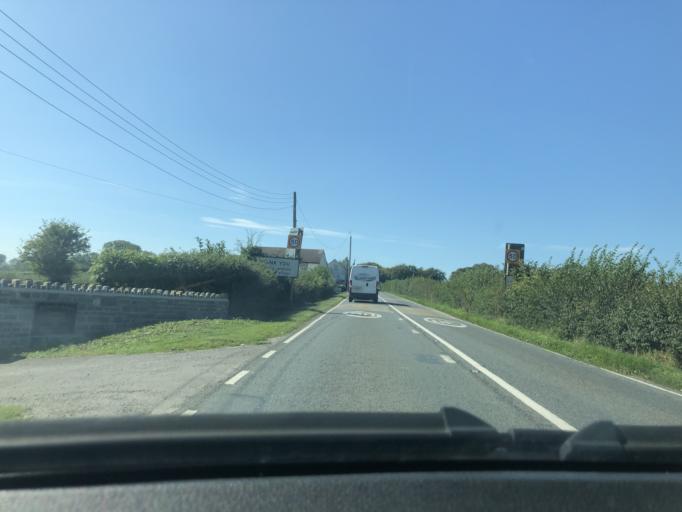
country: GB
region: England
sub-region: Somerset
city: Street
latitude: 51.1302
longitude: -2.8205
